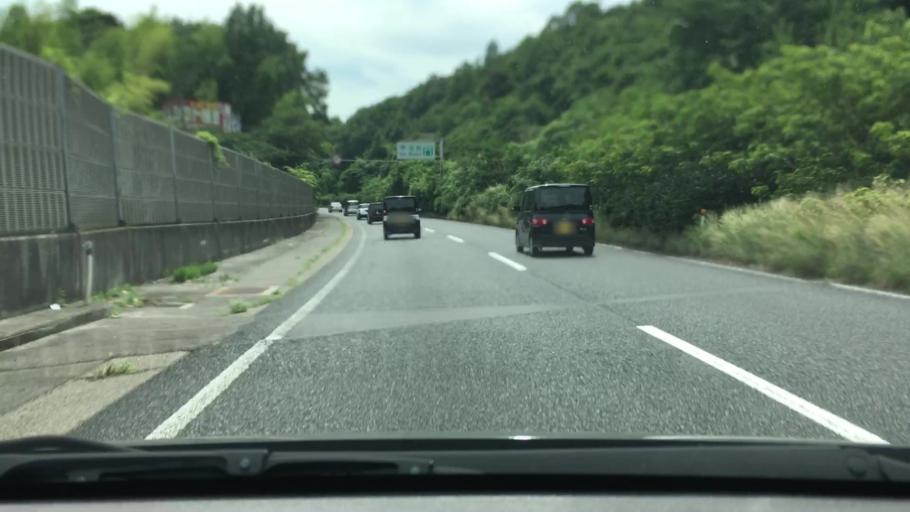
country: JP
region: Hiroshima
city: Hatsukaichi
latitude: 34.3720
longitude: 132.3371
